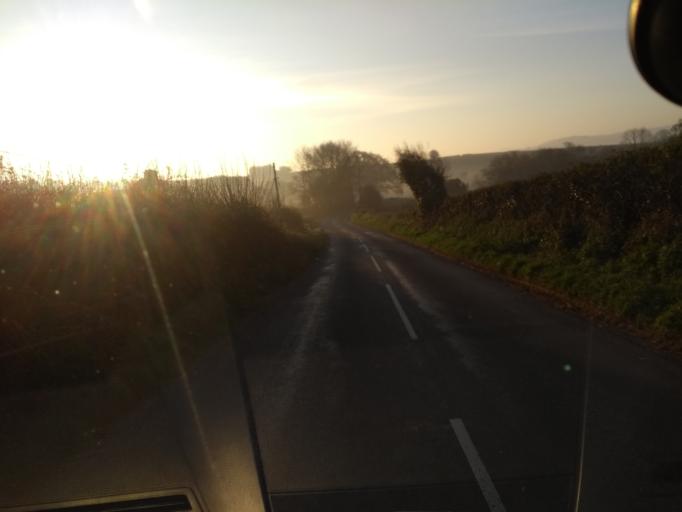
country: GB
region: England
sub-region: Somerset
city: Chard
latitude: 50.8567
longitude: -2.9073
